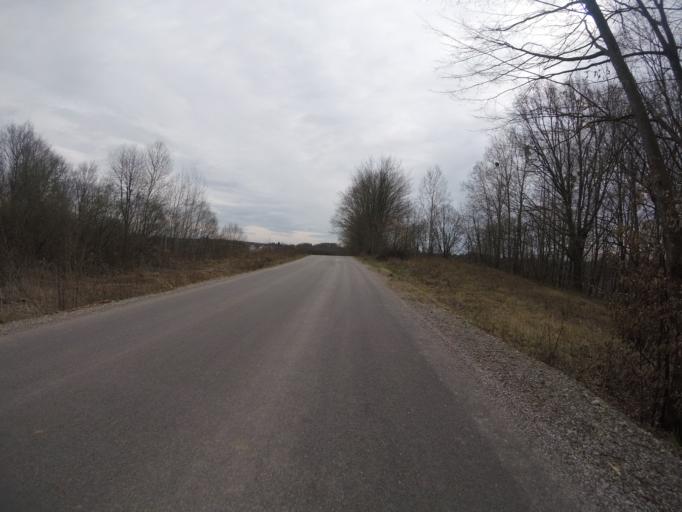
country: HR
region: Grad Zagreb
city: Strmec
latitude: 45.5973
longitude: 15.9125
